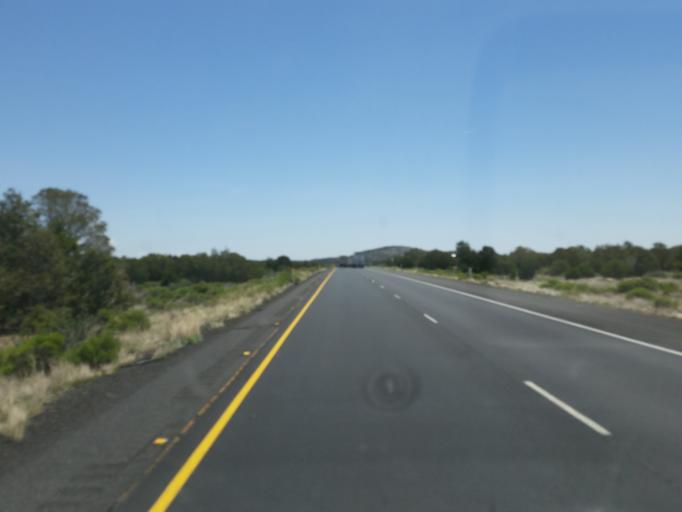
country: US
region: Arizona
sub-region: Coconino County
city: Flagstaff
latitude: 35.2018
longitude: -111.4491
